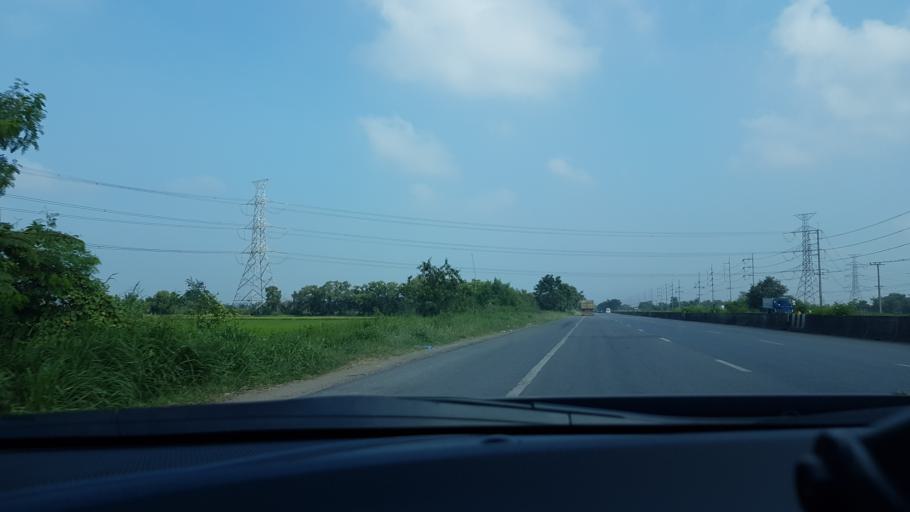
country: TH
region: Pathum Thani
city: Sam Khok
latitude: 14.1291
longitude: 100.5695
